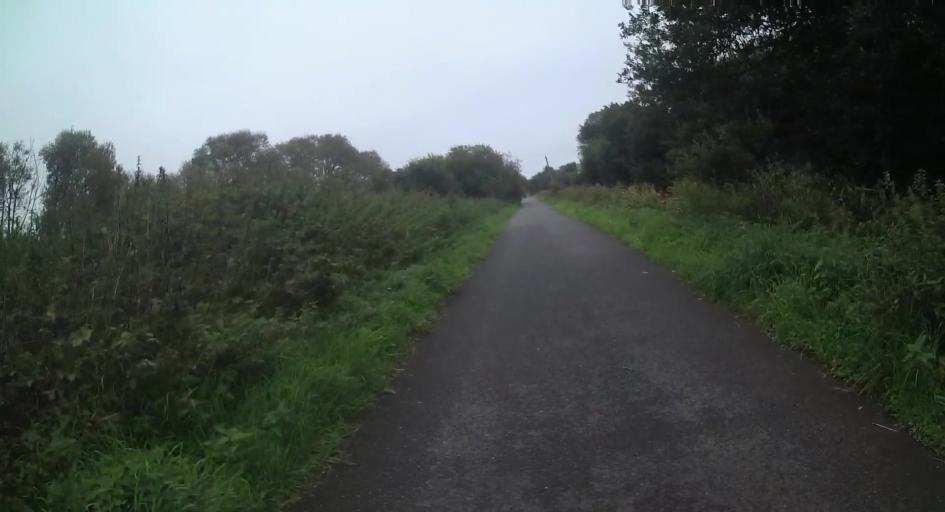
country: GB
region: England
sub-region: Isle of Wight
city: Sandown
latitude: 50.6639
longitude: -1.1740
